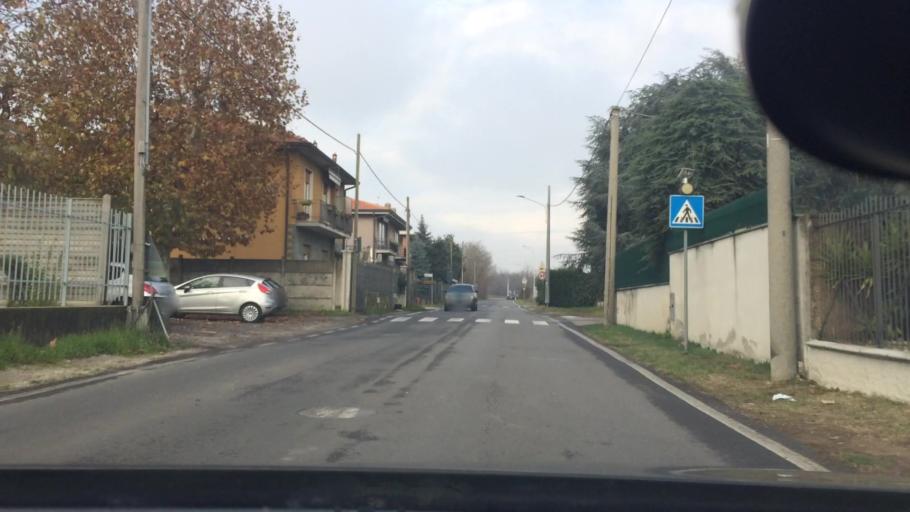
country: IT
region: Lombardy
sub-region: Citta metropolitana di Milano
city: Cerro Maggiore
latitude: 45.6004
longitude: 8.9541
